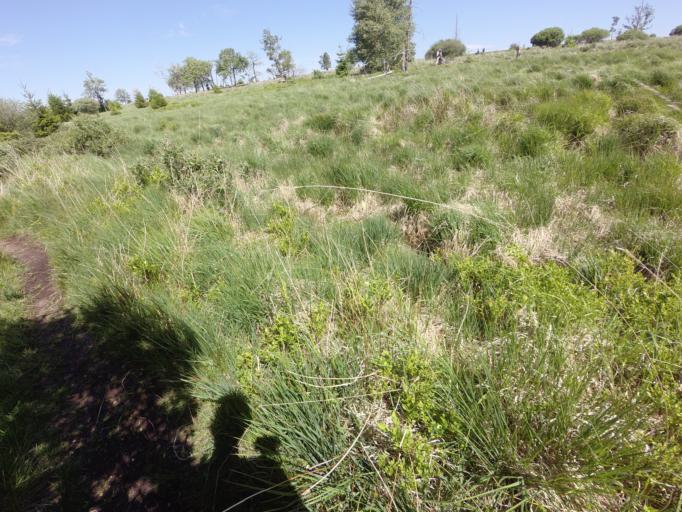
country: BE
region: Wallonia
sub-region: Province de Liege
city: Jalhay
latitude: 50.5138
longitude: 6.0376
